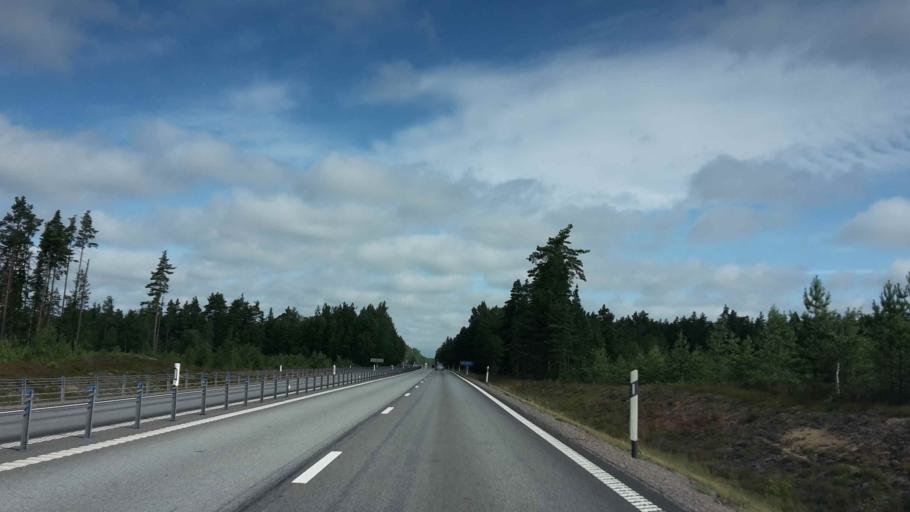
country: SE
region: OErebro
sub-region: Askersunds Kommun
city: Asbro
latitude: 59.0202
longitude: 15.0331
